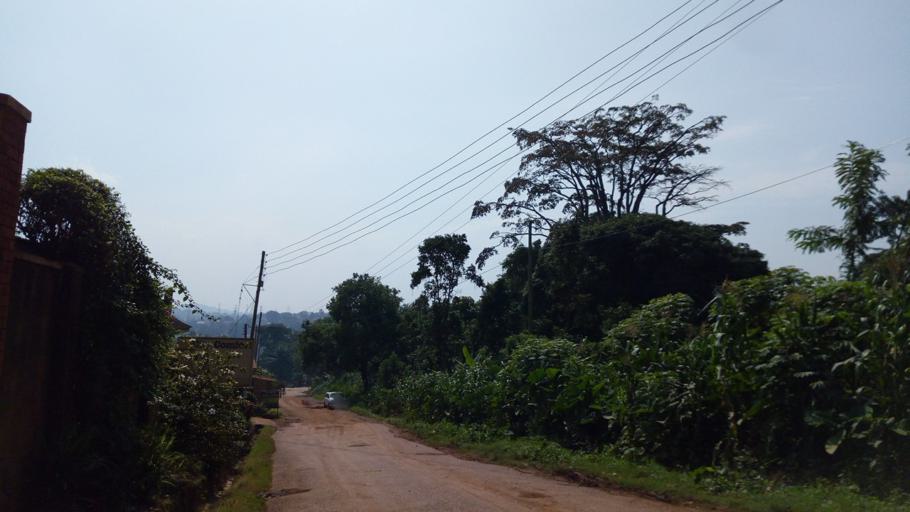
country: UG
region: Central Region
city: Kampala Central Division
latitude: 0.3412
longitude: 32.5664
